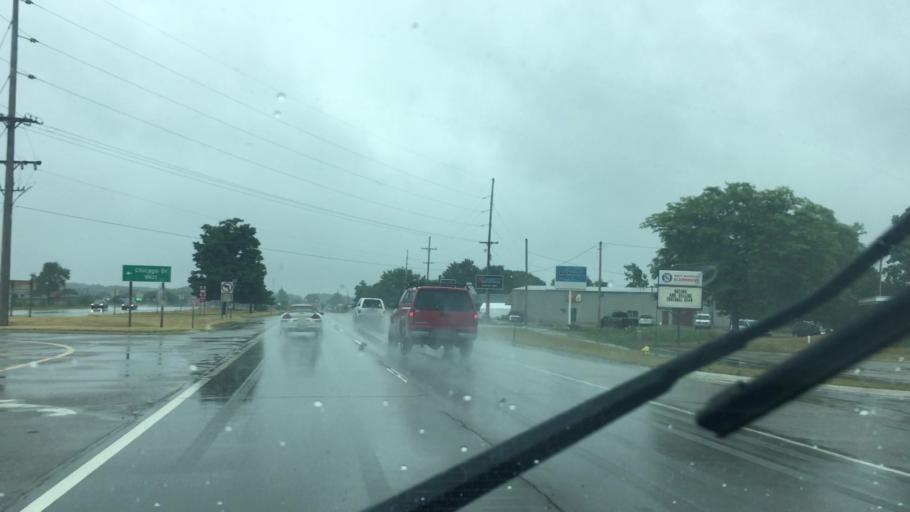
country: US
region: Michigan
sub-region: Ottawa County
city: Jenison
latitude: 42.9006
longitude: -85.7983
